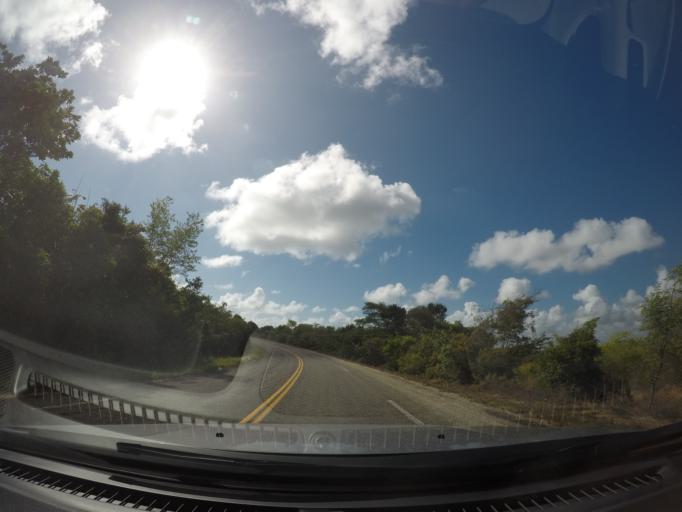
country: BR
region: Paraiba
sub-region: Conde
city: Conde
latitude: -7.3388
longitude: -34.8098
